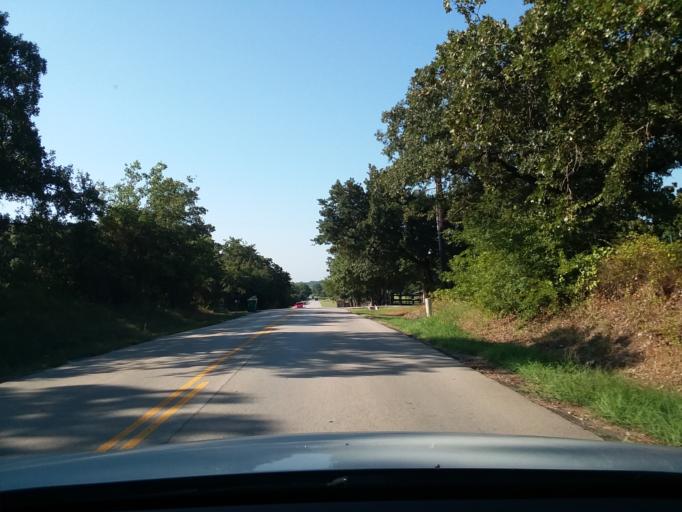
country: US
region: Texas
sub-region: Denton County
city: Bartonville
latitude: 33.0643
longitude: -97.1316
